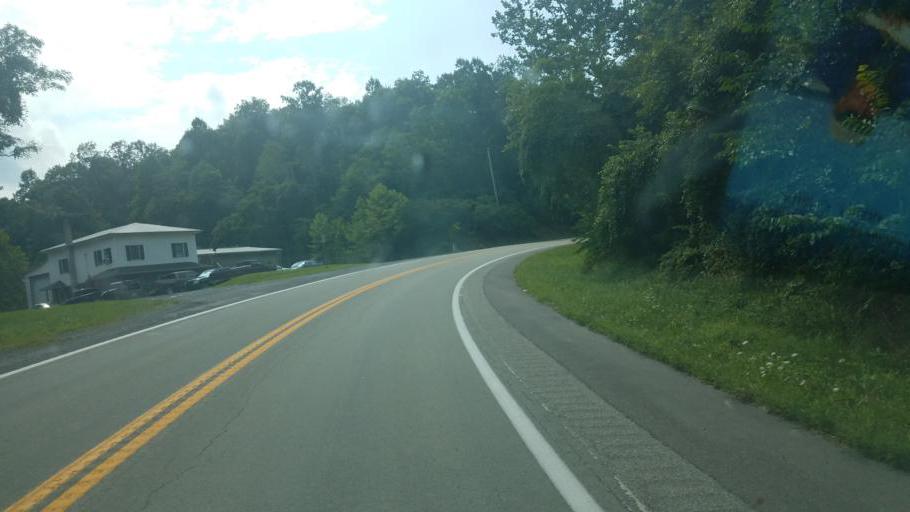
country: US
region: Virginia
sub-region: Frederick County
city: Shawnee Land
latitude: 39.3574
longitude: -78.3676
